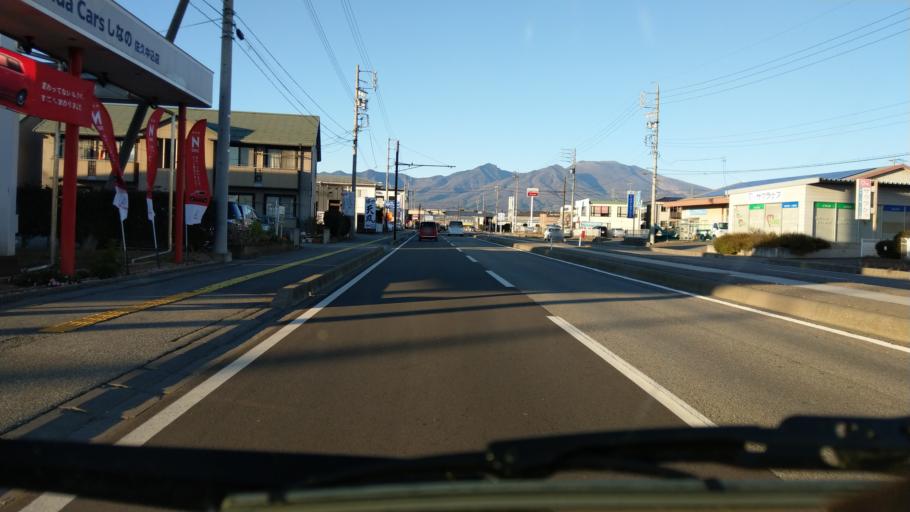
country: JP
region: Nagano
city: Saku
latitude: 36.2525
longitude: 138.4676
